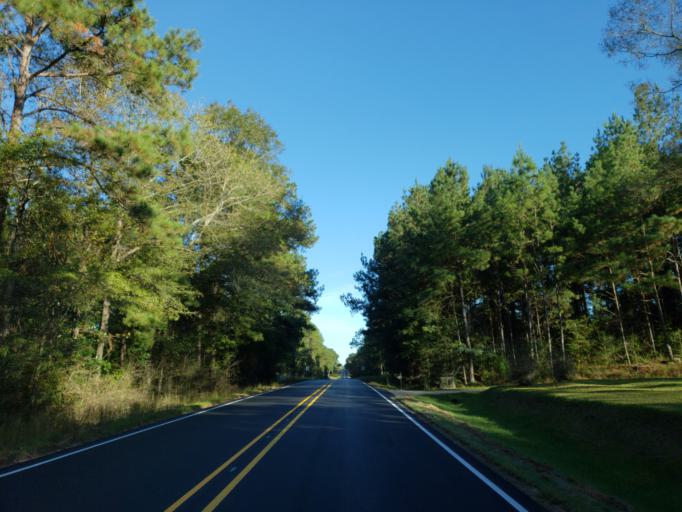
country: US
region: Mississippi
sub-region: Perry County
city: Richton
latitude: 31.3614
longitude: -88.8014
